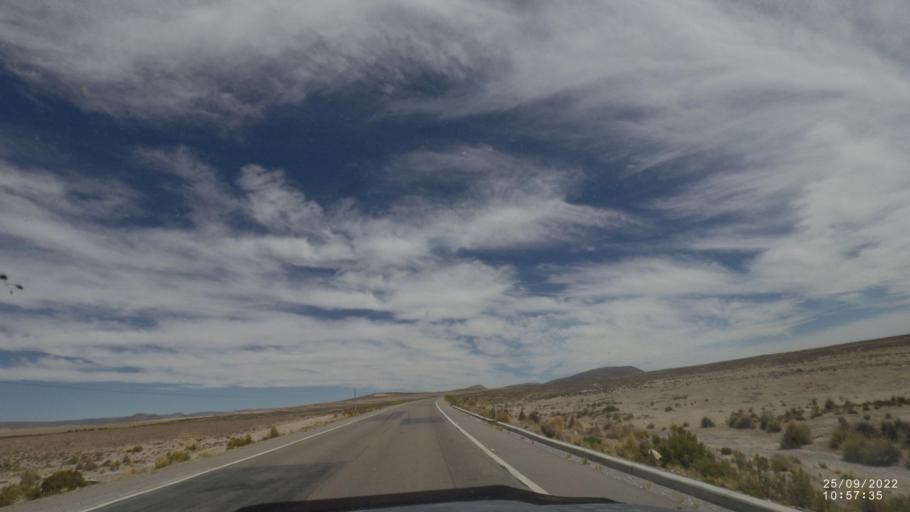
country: BO
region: Oruro
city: Challapata
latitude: -19.4734
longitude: -66.8937
